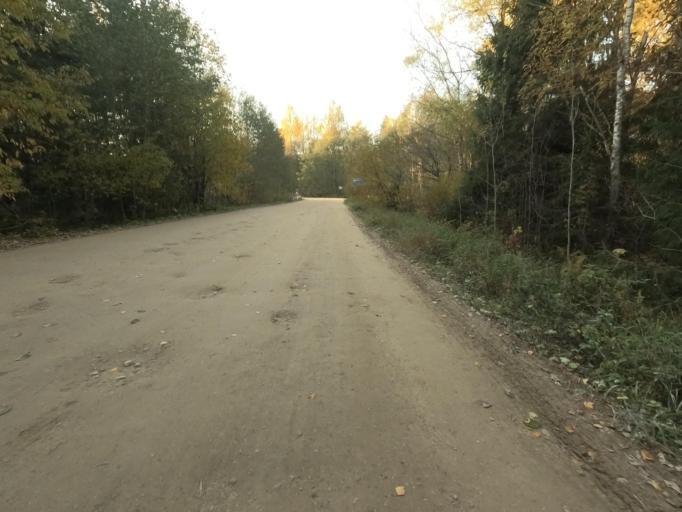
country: RU
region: Leningrad
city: Lyuban'
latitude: 59.0155
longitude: 31.0845
